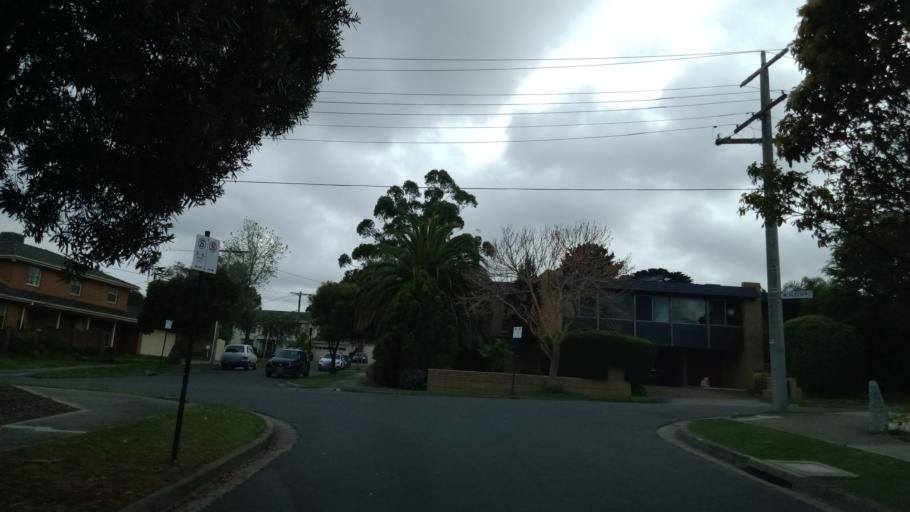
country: AU
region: Victoria
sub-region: Monash
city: Notting Hill
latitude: -37.8766
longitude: 145.1344
